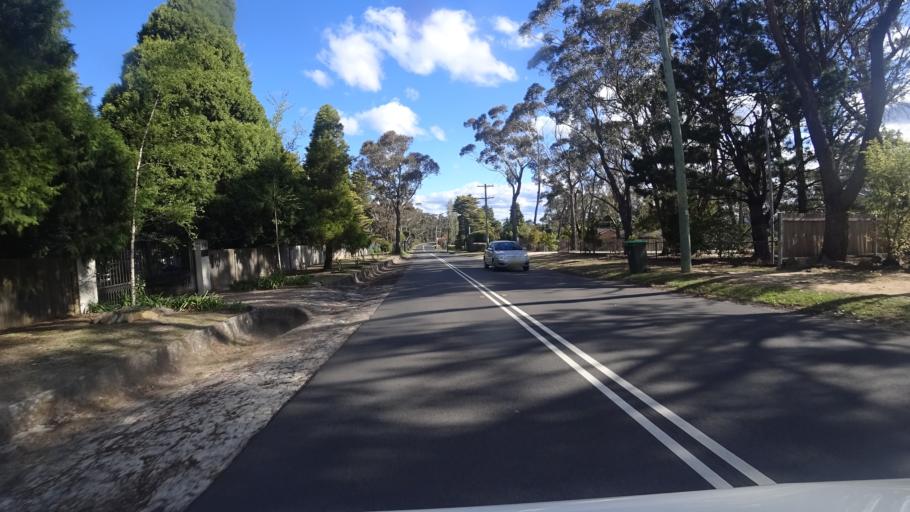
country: AU
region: New South Wales
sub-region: Blue Mountains Municipality
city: Katoomba
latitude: -33.7192
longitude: 150.2939
